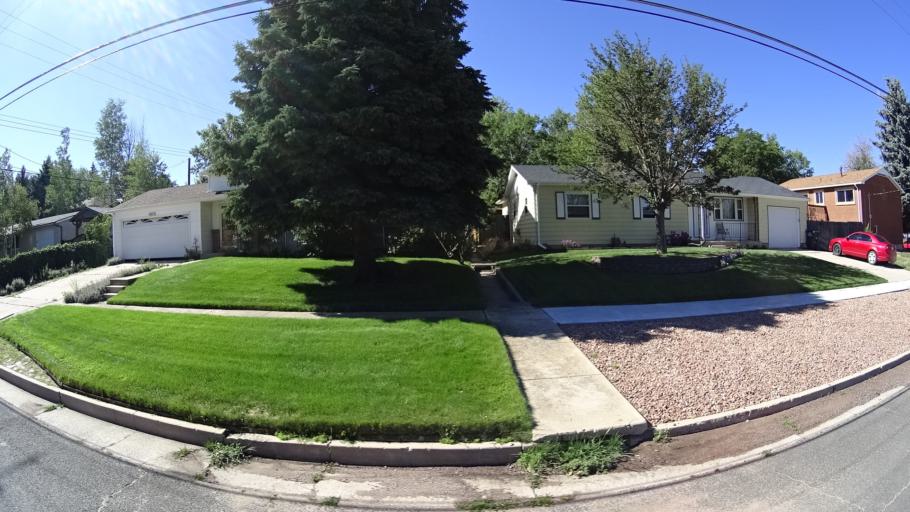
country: US
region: Colorado
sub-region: El Paso County
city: Colorado Springs
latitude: 38.8677
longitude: -104.7880
